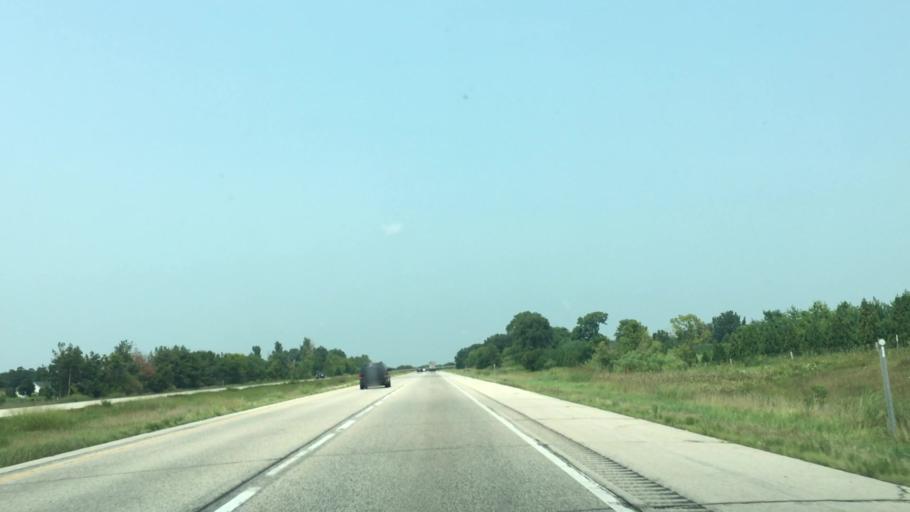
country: US
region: Iowa
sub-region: Linn County
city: Robins
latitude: 42.1175
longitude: -91.7120
